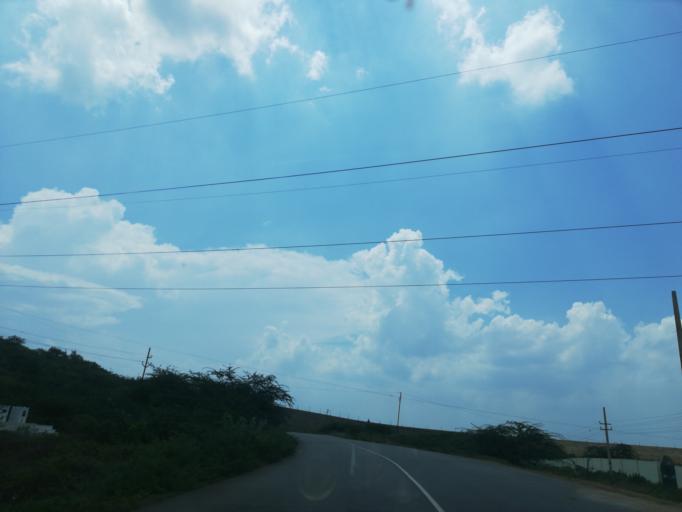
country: IN
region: Andhra Pradesh
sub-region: Guntur
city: Macherla
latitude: 16.5958
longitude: 79.3130
